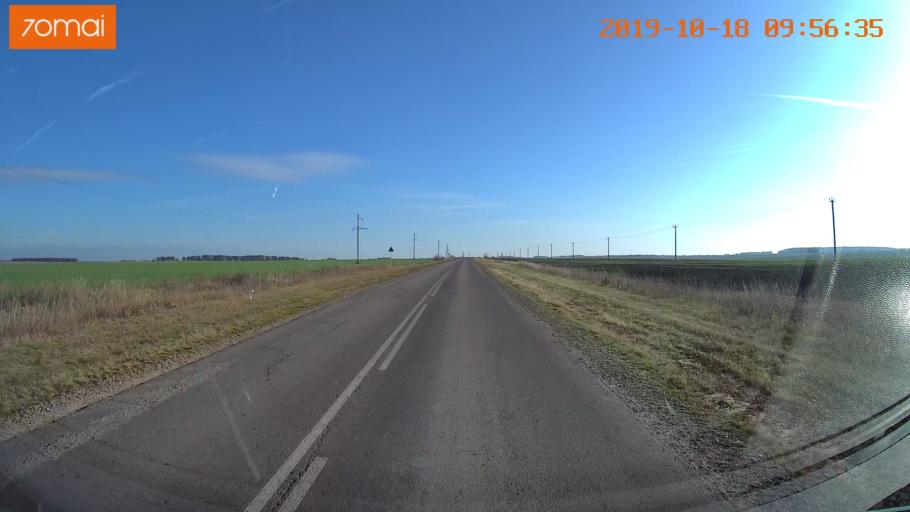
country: RU
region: Tula
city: Kurkino
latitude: 53.3747
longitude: 38.3935
